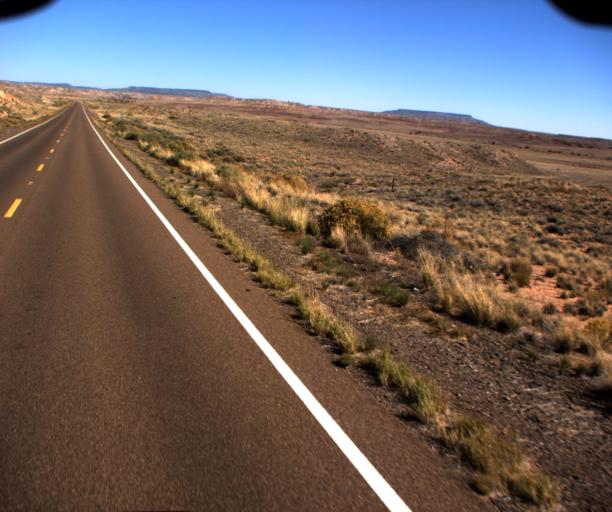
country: US
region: Arizona
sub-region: Navajo County
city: Joseph City
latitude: 35.1620
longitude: -110.4569
